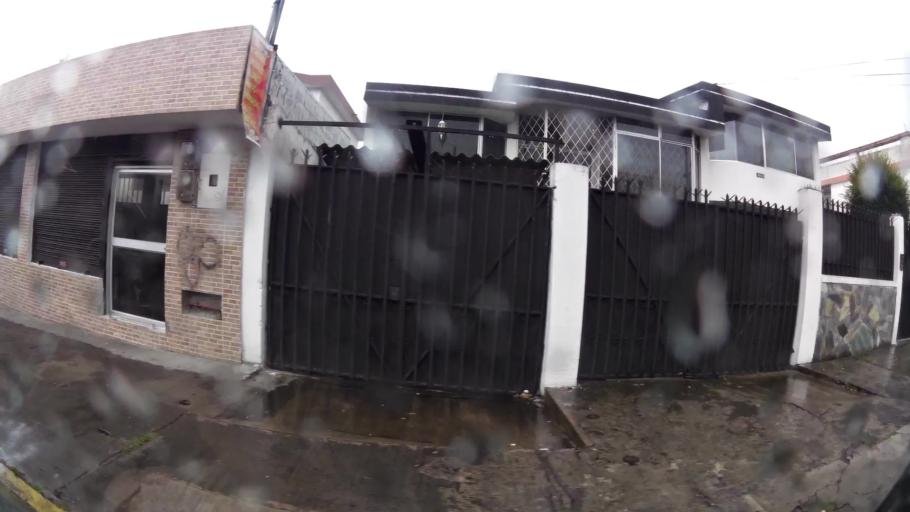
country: EC
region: Pichincha
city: Quito
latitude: -0.1124
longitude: -78.4977
